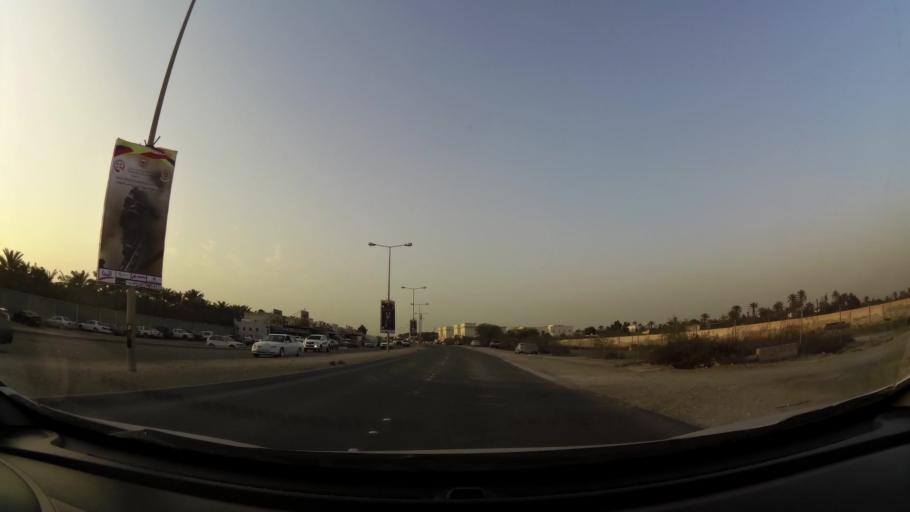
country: BH
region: Northern
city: Madinat `Isa
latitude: 26.1884
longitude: 50.4659
